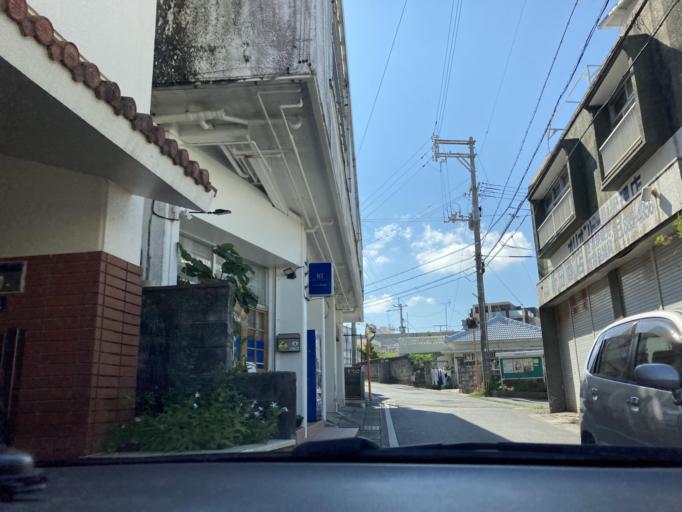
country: JP
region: Okinawa
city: Naha-shi
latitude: 26.2243
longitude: 127.7293
